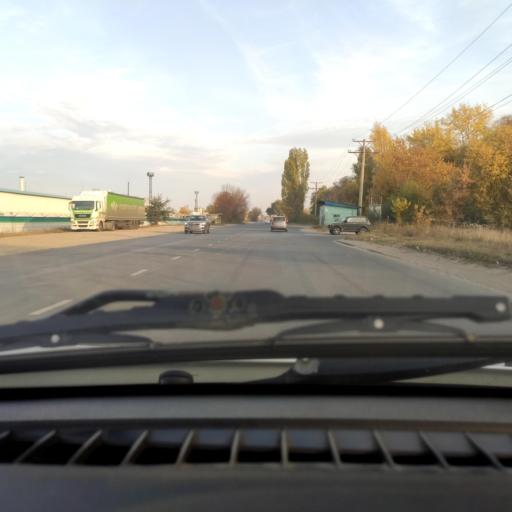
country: RU
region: Samara
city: Tol'yatti
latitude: 53.5329
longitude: 49.4519
